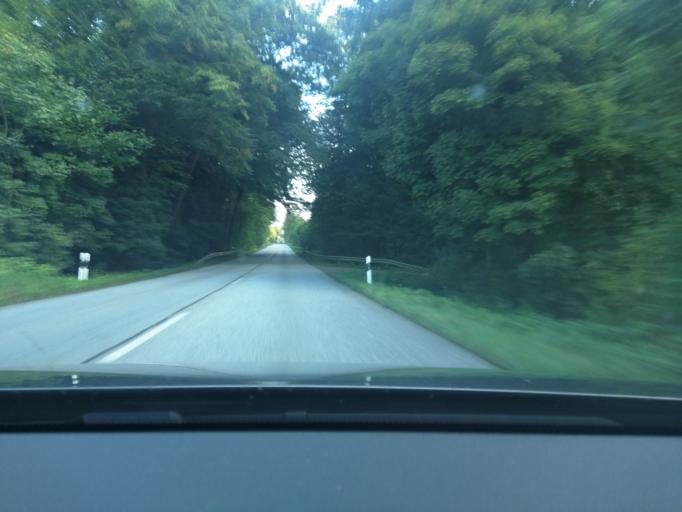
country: DE
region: Schleswig-Holstein
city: Grabau
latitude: 53.4811
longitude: 10.5284
